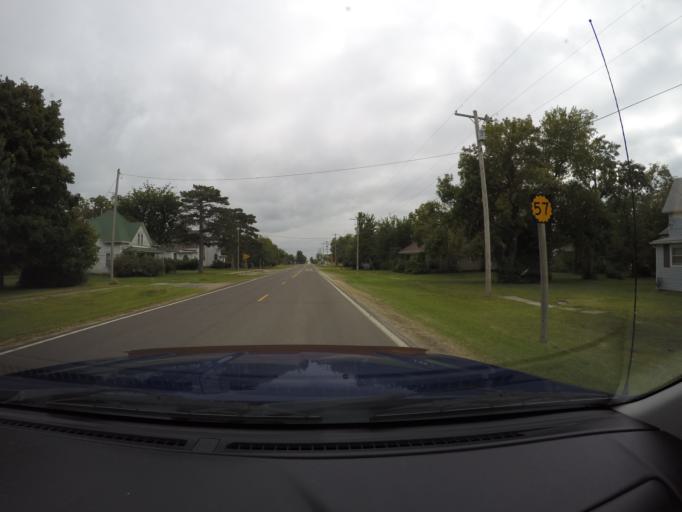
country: US
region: Kansas
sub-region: Morris County
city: Council Grove
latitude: 38.8458
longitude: -96.5940
